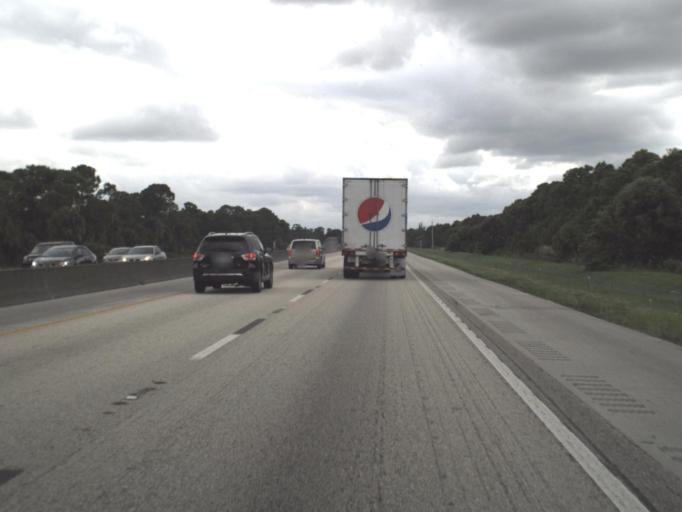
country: US
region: Florida
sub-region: Palm Beach County
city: Palm Beach Gardens
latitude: 26.7811
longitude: -80.1326
